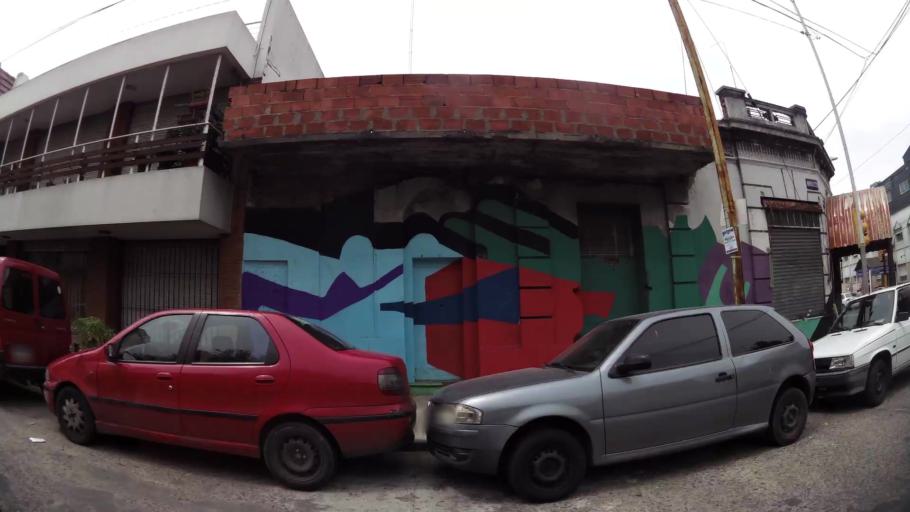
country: AR
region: Buenos Aires
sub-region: Partido de Avellaneda
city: Avellaneda
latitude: -34.6610
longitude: -58.3705
